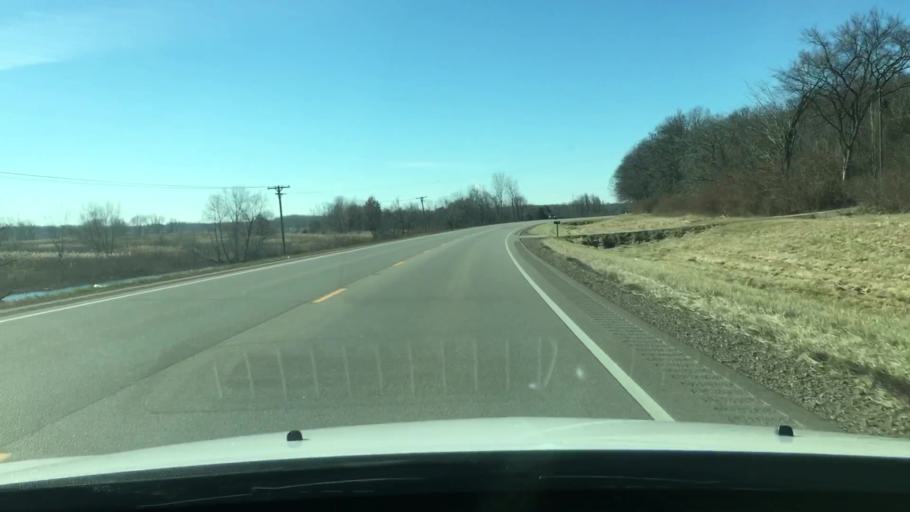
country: US
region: Illinois
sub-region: Peoria County
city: Glasford
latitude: 40.5238
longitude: -89.8820
